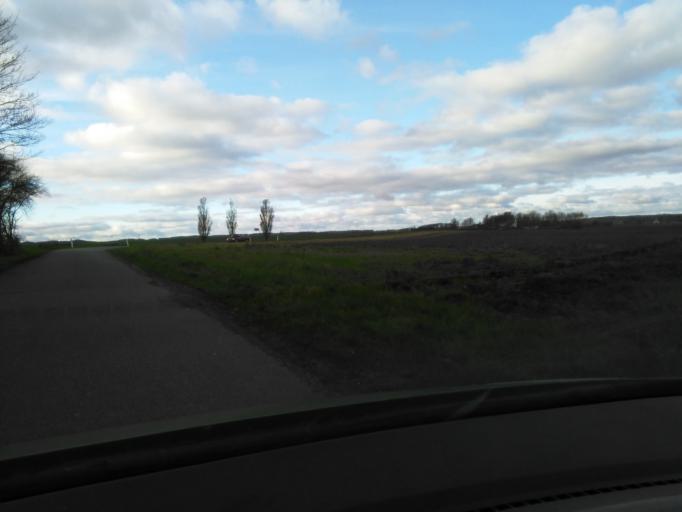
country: DK
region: Central Jutland
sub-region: Odder Kommune
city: Odder
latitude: 55.8919
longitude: 10.1643
